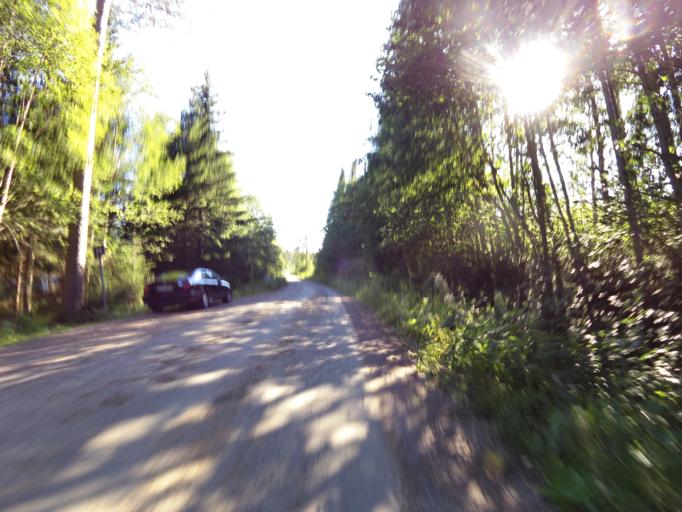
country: SE
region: Gaevleborg
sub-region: Hofors Kommun
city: Hofors
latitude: 60.6004
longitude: 16.2781
